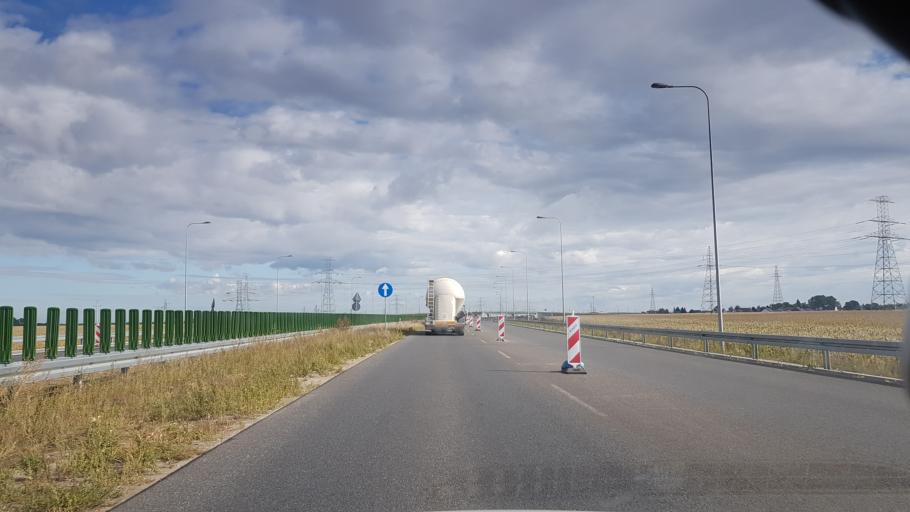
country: PL
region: Greater Poland Voivodeship
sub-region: Powiat poznanski
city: Steszew
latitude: 52.3290
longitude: 16.7256
